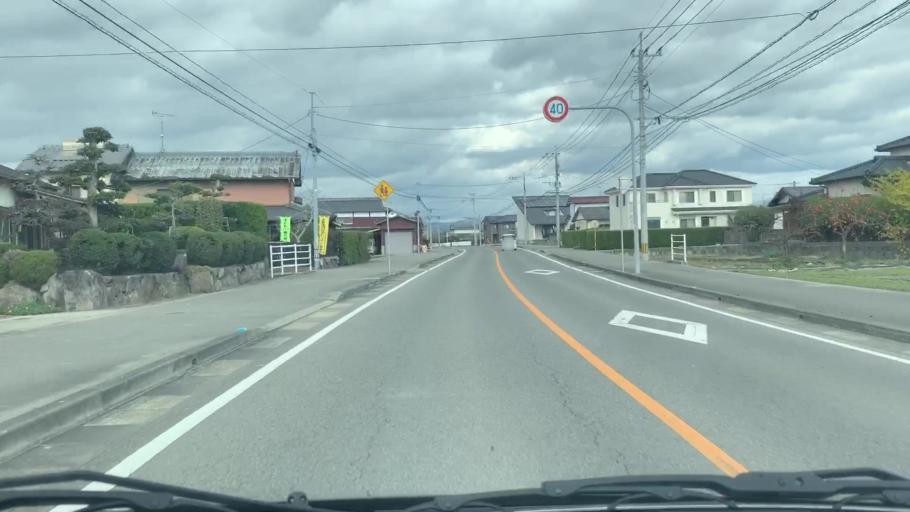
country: JP
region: Saga Prefecture
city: Saga-shi
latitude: 33.2438
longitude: 130.2376
